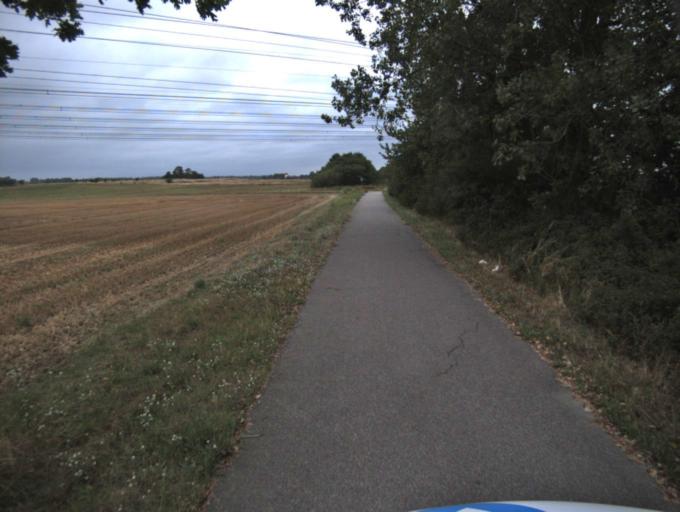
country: SE
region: Skane
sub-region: Kavlinge Kommun
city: Hofterup
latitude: 55.7747
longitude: 12.9869
